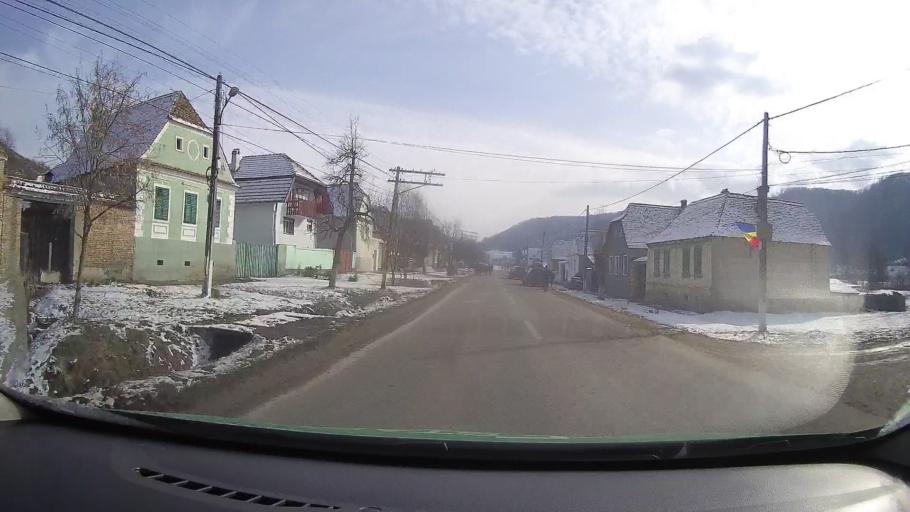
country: RO
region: Mures
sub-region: Comuna Apold
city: Saes
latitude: 46.1543
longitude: 24.7699
